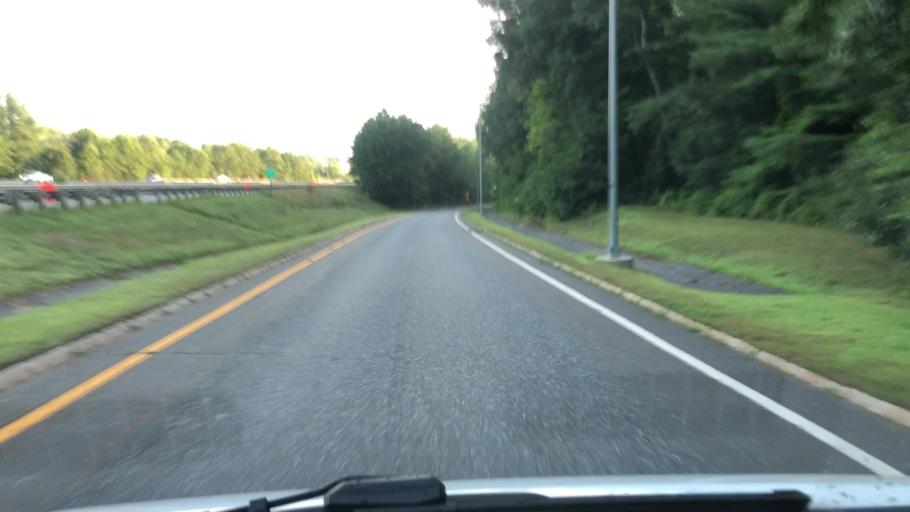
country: US
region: Massachusetts
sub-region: Franklin County
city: Greenfield
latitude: 42.5817
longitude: -72.6214
